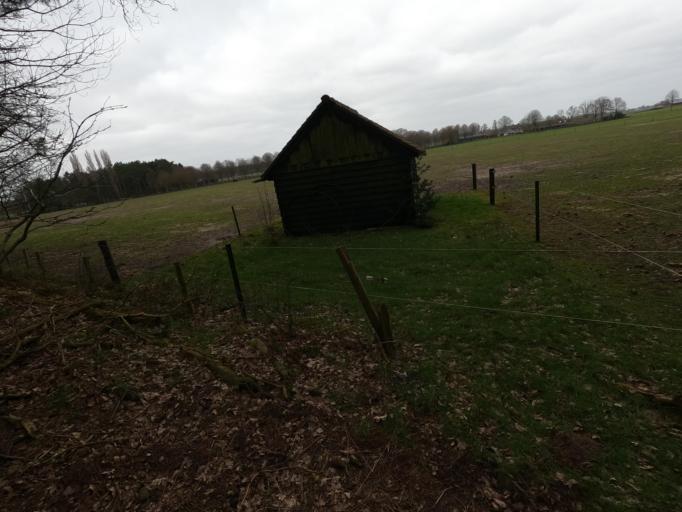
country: NL
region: North Brabant
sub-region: Gemeente Woensdrecht
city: Woensdrecht
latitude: 51.4196
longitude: 4.3906
